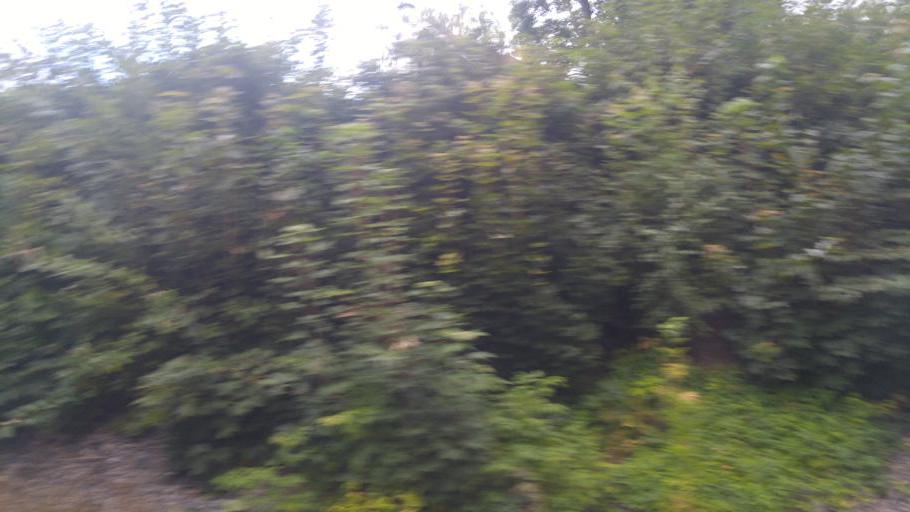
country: NO
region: Oslo
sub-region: Oslo
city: Sjolyststranda
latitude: 59.9561
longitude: 10.6959
